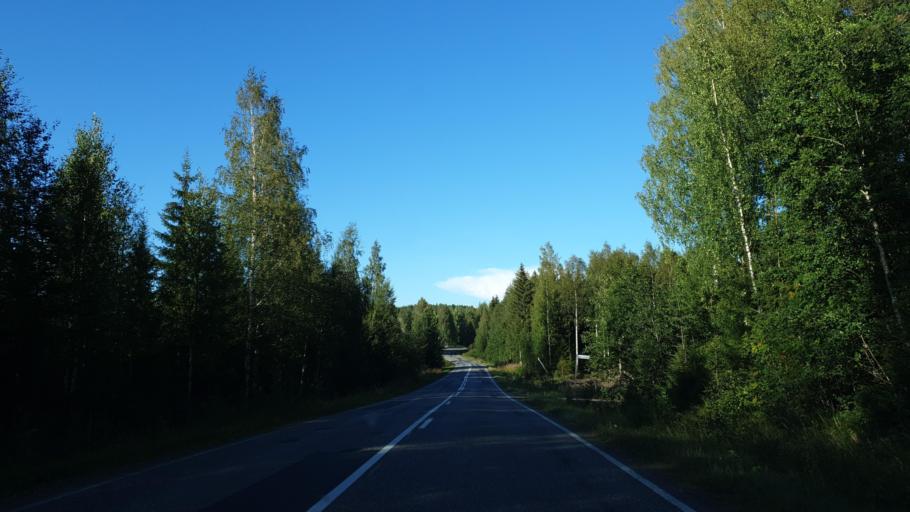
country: FI
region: Northern Savo
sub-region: Koillis-Savo
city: Juankoski
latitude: 63.0923
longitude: 28.4160
